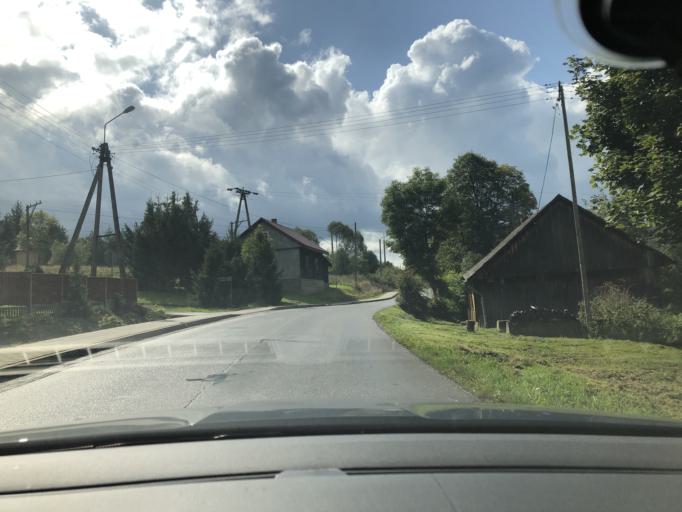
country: PL
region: Lesser Poland Voivodeship
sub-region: Powiat suski
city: Lachowice
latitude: 49.7089
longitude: 19.4650
